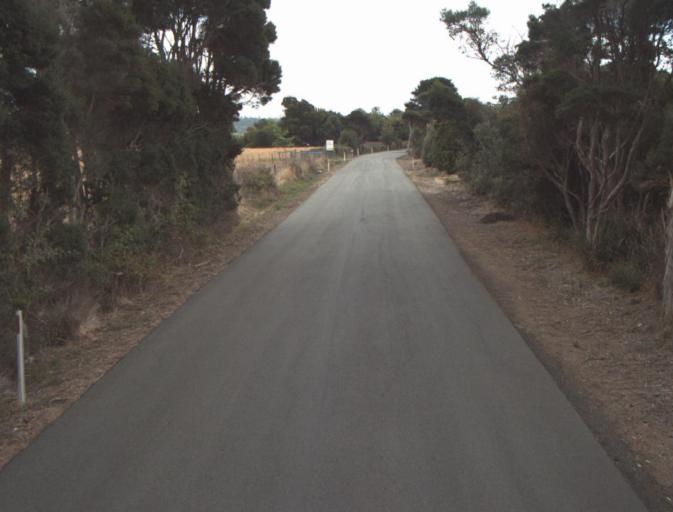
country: AU
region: Tasmania
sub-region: Launceston
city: Mayfield
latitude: -41.2840
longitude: 147.0052
